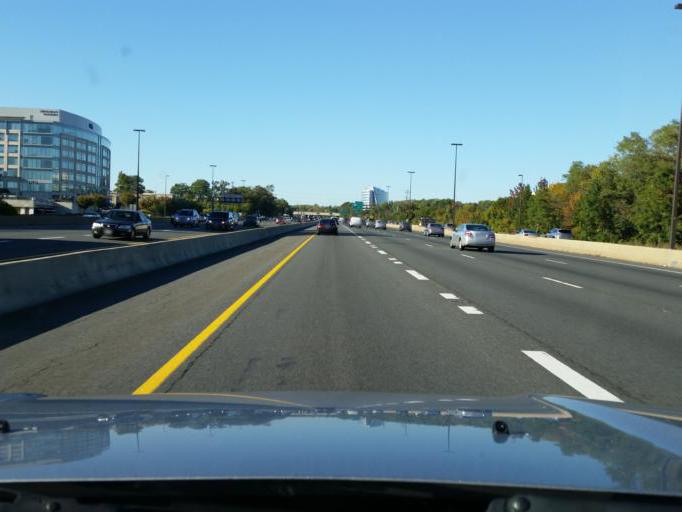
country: US
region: Maryland
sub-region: Montgomery County
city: Rockville
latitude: 39.0580
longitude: -77.1548
